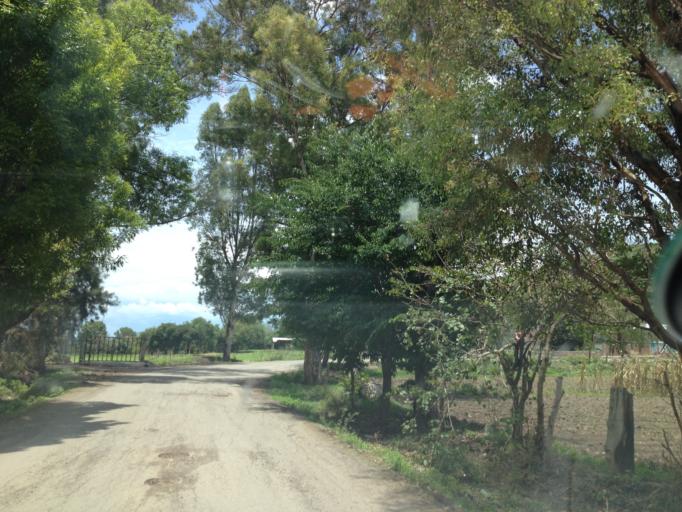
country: MX
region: Michoacan
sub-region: Tarimbaro
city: El Colegio
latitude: 19.7747
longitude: -101.1799
